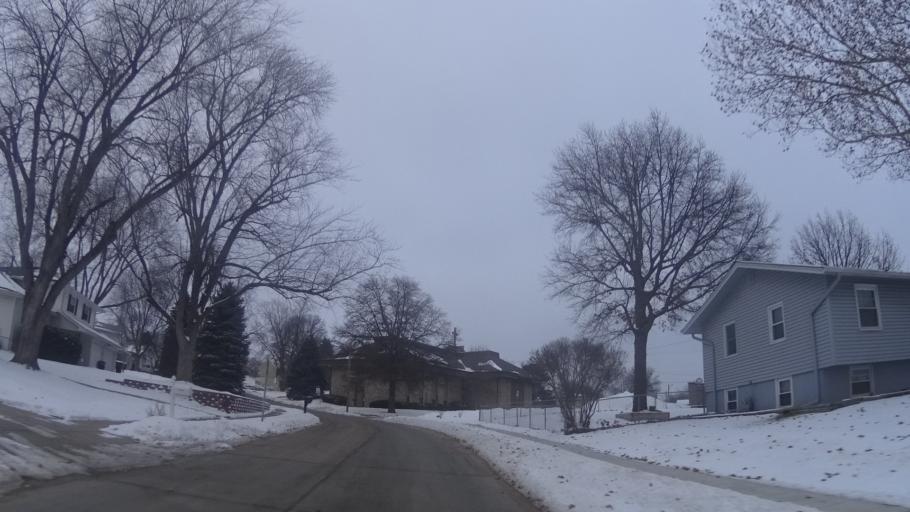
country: US
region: Nebraska
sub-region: Sarpy County
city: Offutt Air Force Base
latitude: 41.1465
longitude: -95.9245
